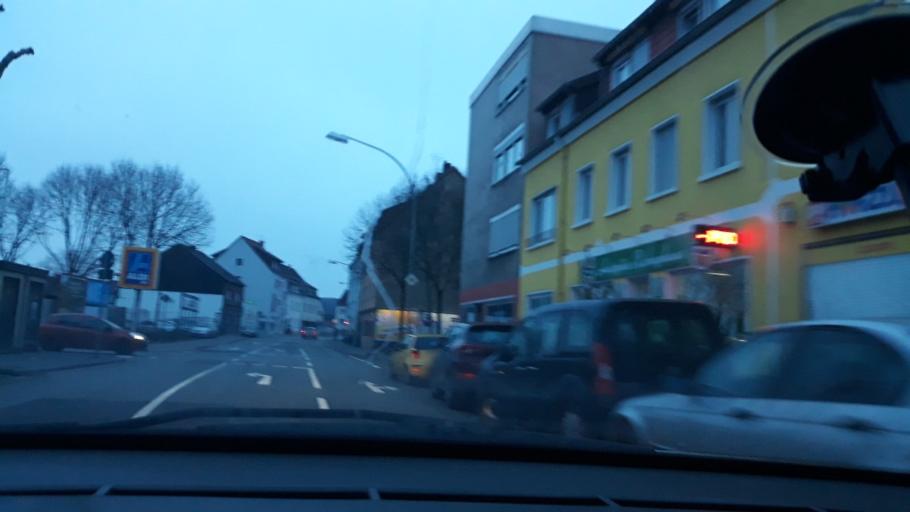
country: FR
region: Lorraine
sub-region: Departement de la Moselle
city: Schoeneck
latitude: 49.2453
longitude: 6.9427
